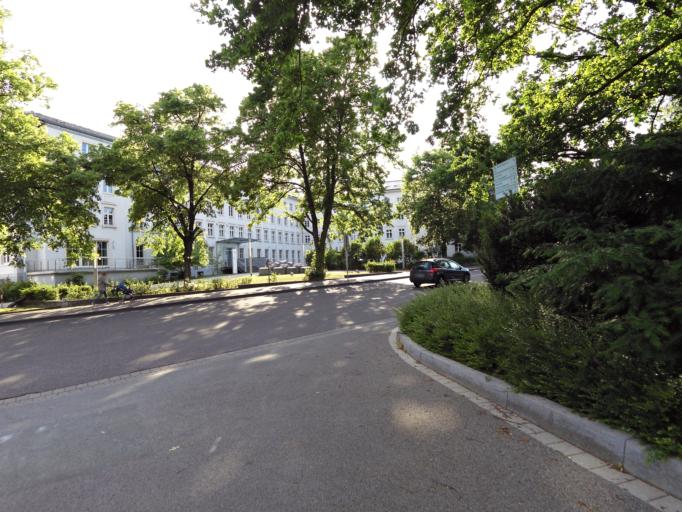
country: DE
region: Rheinland-Pfalz
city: Koblenz
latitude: 50.3530
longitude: 7.5993
